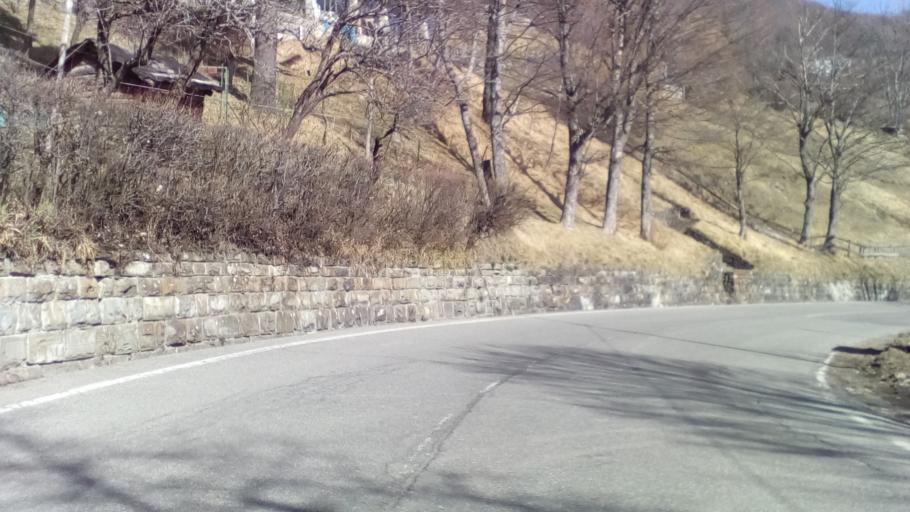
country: IT
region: Emilia-Romagna
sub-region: Provincia di Modena
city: Riolunato
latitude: 44.2655
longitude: 10.6516
